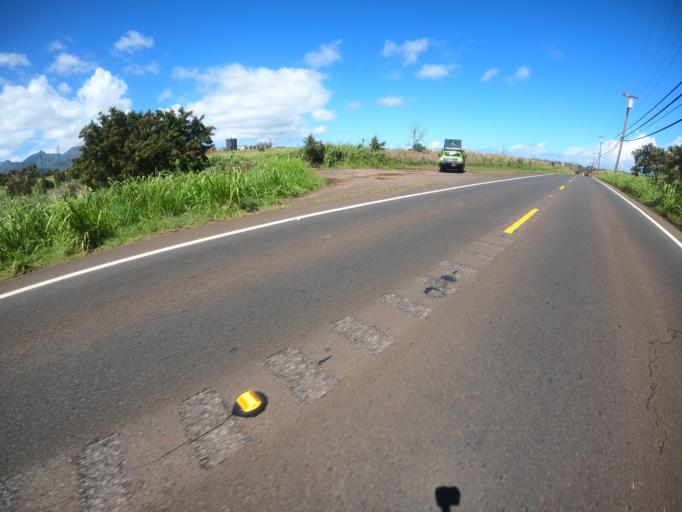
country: US
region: Hawaii
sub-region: Honolulu County
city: Schofield Barracks
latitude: 21.4709
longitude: -158.0529
